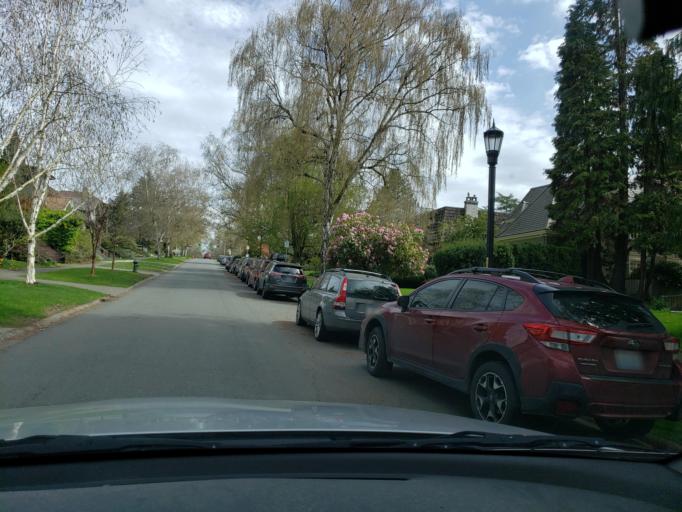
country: US
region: Washington
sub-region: King County
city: Seattle
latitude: 47.6464
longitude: -122.3070
